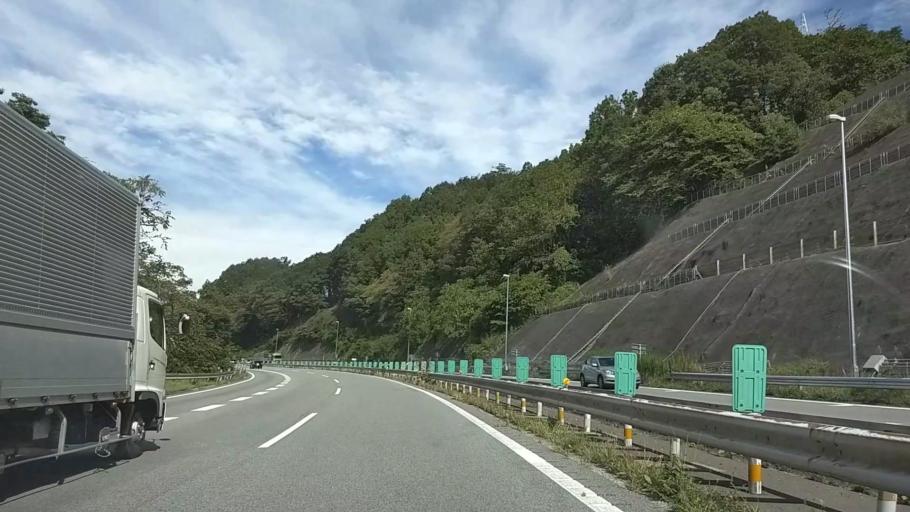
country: JP
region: Yamanashi
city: Nirasaki
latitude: 35.7902
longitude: 138.4093
